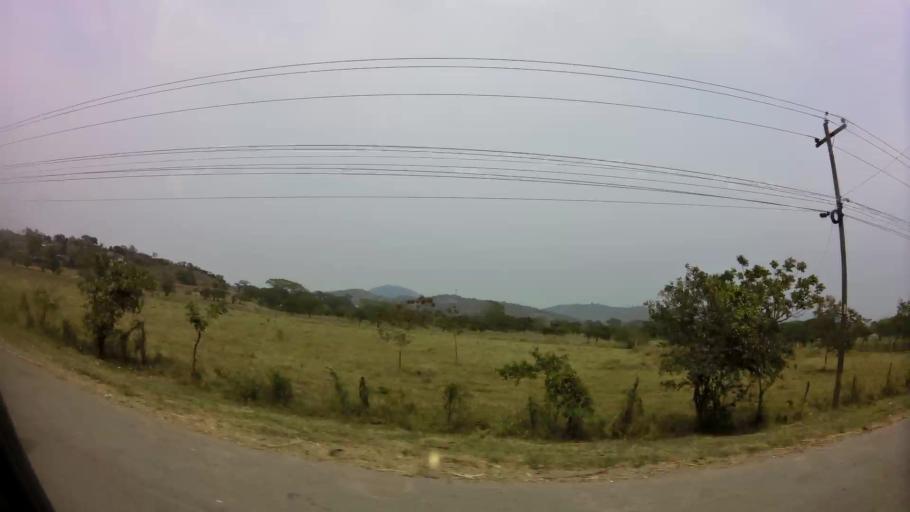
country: HN
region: Cortes
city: Nuevo Chamelecon
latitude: 15.3759
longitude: -87.9873
